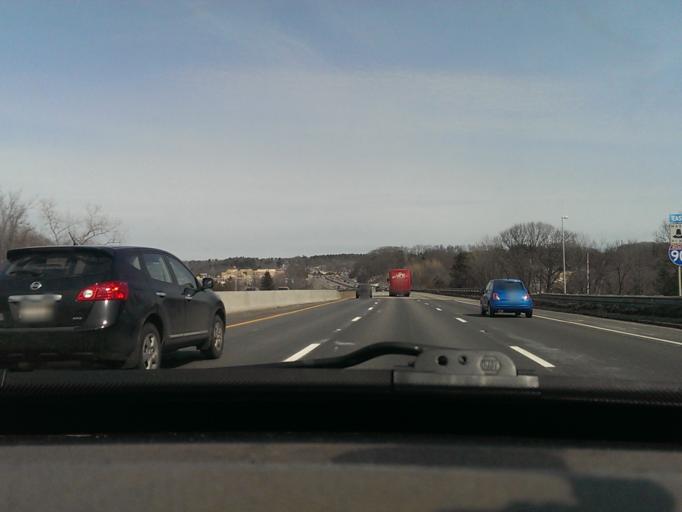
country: US
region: Massachusetts
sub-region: Worcester County
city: Auburn
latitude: 42.1948
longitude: -71.8470
